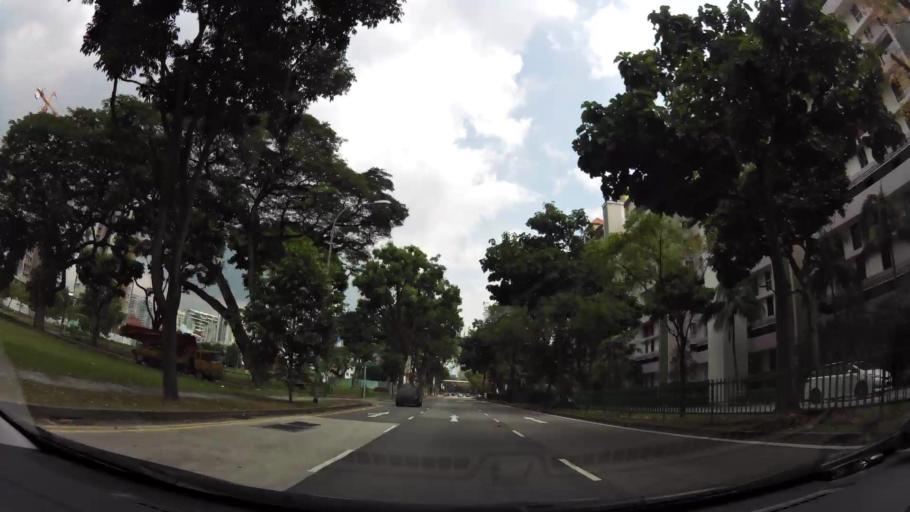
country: SG
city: Singapore
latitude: 1.2911
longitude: 103.8213
